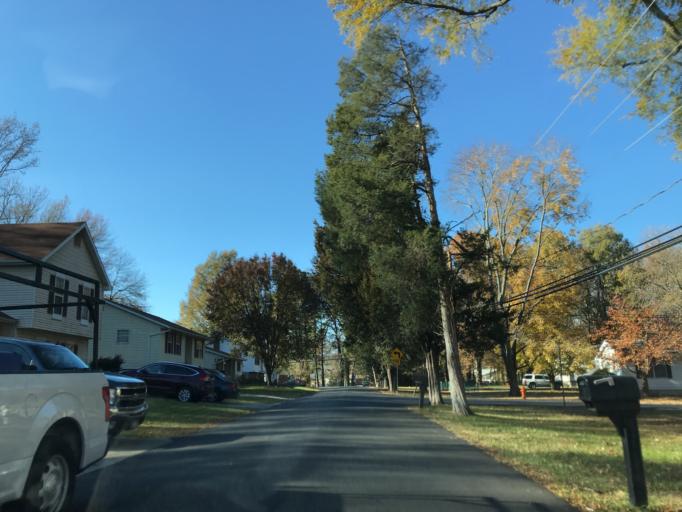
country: US
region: Maryland
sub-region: Baltimore County
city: Bowleys Quarters
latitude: 39.3720
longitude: -76.3550
